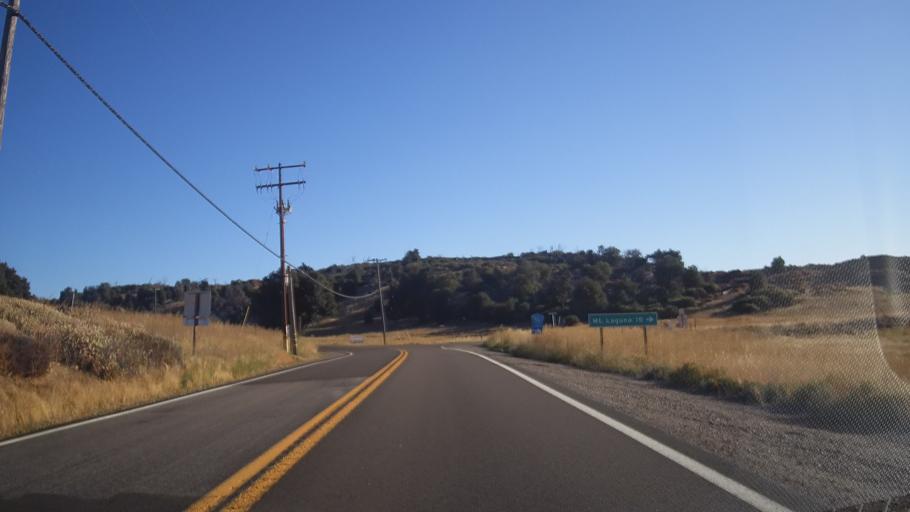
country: US
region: California
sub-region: San Diego County
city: Julian
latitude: 33.0105
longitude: -116.5621
